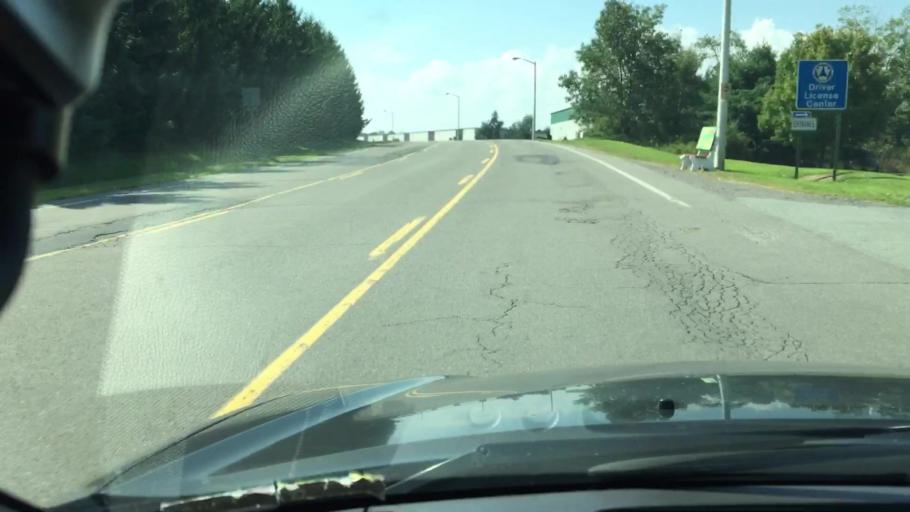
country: US
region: Pennsylvania
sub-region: Luzerne County
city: Ashley
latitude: 41.2009
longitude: -75.9303
